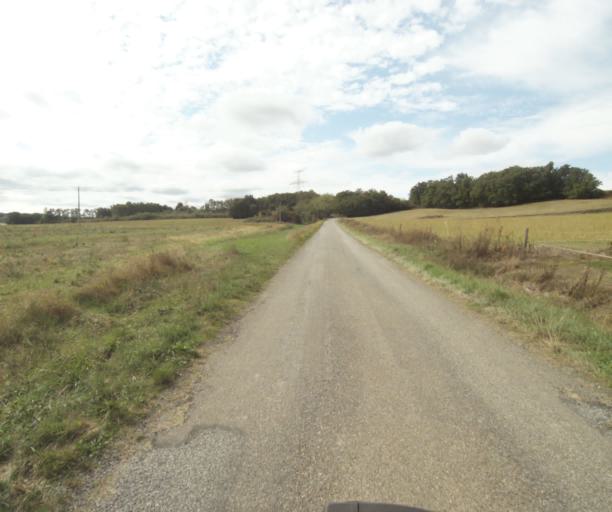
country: FR
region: Midi-Pyrenees
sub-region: Departement du Tarn-et-Garonne
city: Verdun-sur-Garonne
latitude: 43.8629
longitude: 1.1953
